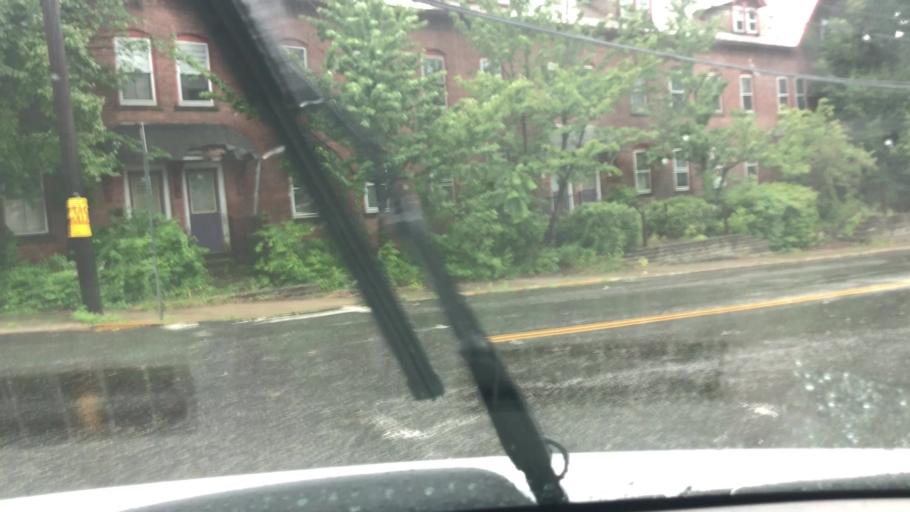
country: US
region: Massachusetts
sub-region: Berkshire County
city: Adams
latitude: 42.6187
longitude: -73.1180
